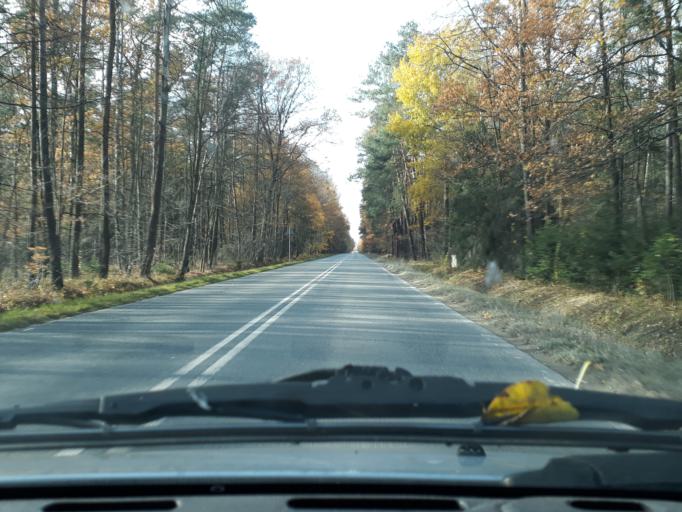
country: PL
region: Silesian Voivodeship
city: Wozniki
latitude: 50.5755
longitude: 19.0226
